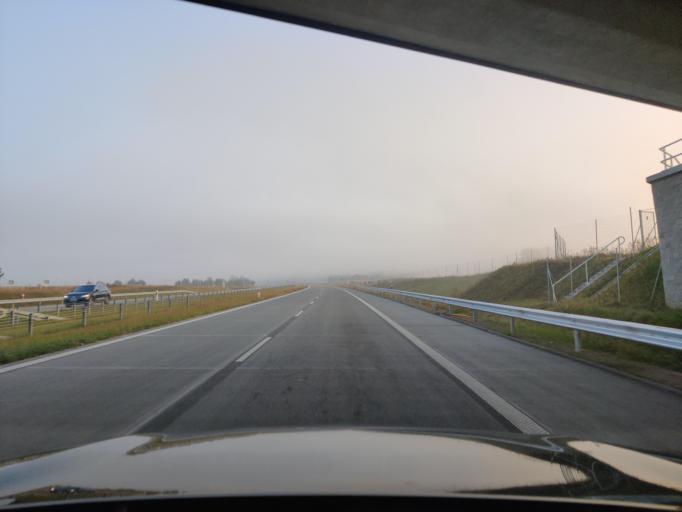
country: PL
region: Masovian Voivodeship
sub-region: Powiat mlawski
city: Mlawa
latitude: 53.1388
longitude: 20.4245
